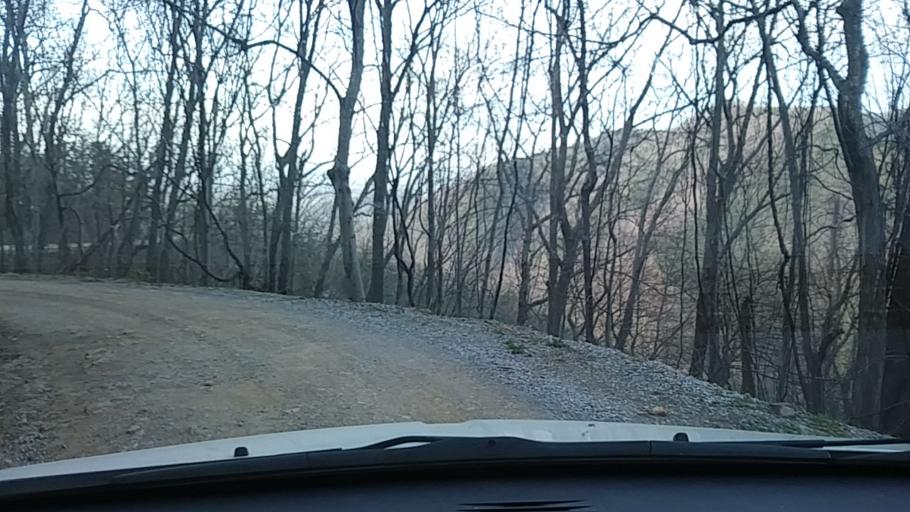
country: US
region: Tennessee
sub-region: Greene County
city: Tusculum
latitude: 36.0861
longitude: -82.6852
